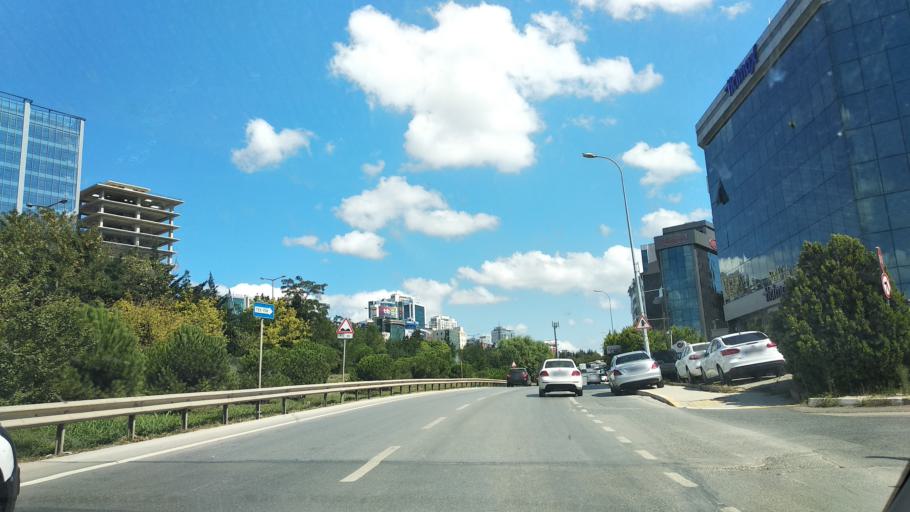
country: TR
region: Istanbul
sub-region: Atasehir
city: Atasehir
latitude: 40.9966
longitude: 29.1337
